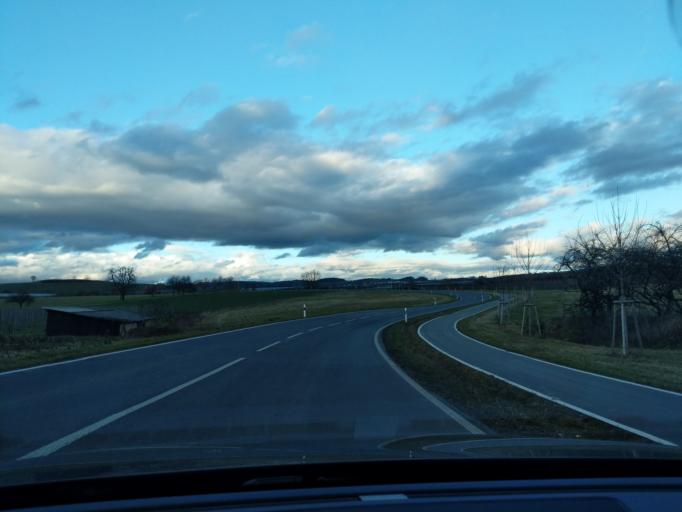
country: DE
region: Baden-Wuerttemberg
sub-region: Tuebingen Region
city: Bermatingen
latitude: 47.7290
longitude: 9.3147
